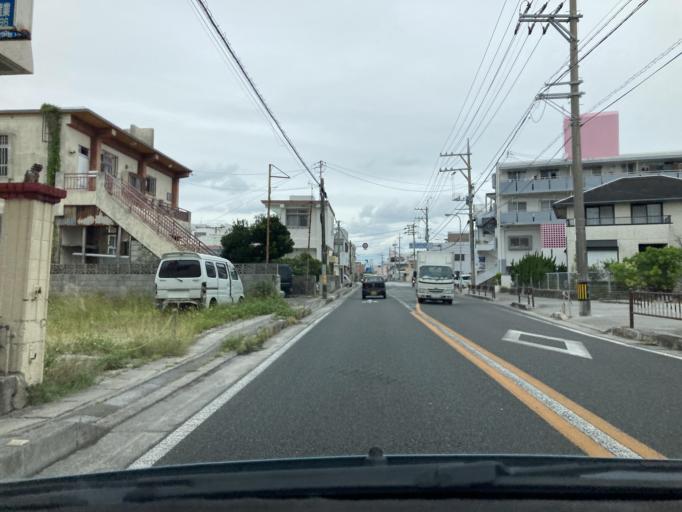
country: JP
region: Okinawa
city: Itoman
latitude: 26.1245
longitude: 127.6698
